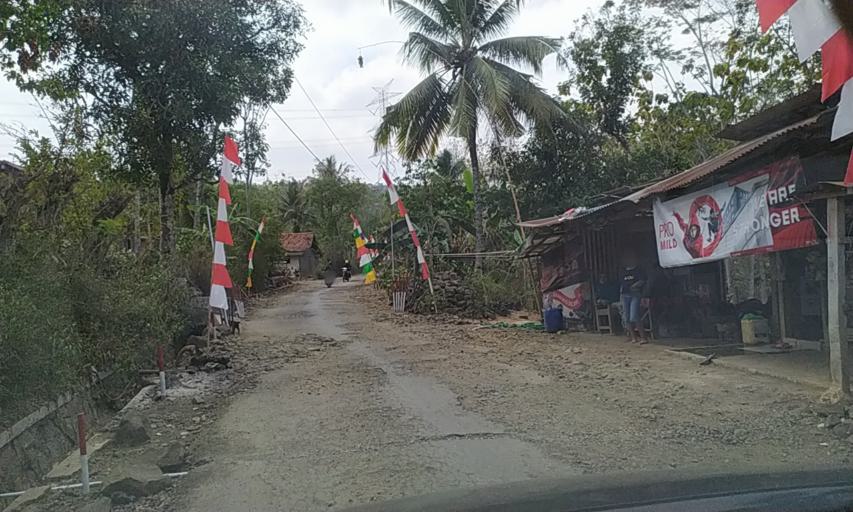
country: ID
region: Central Java
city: Watuagung
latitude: -7.5875
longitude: 109.1154
